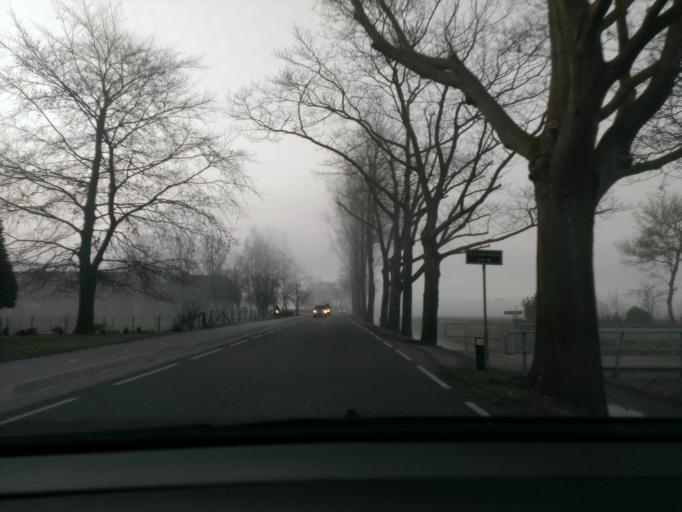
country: NL
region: Gelderland
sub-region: Gemeente Epe
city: Oene
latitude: 52.2856
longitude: 6.0391
